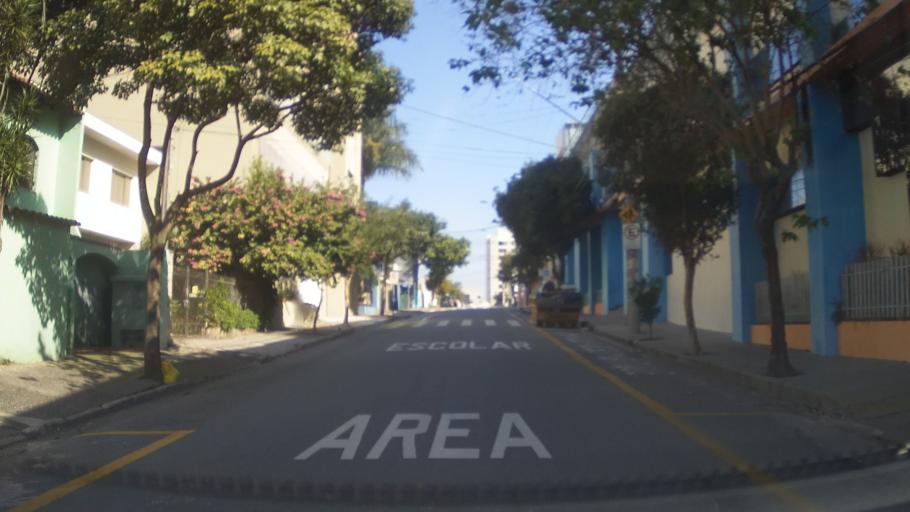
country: BR
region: Sao Paulo
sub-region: Sao Caetano Do Sul
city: Sao Caetano do Sul
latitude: -23.6203
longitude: -46.5614
